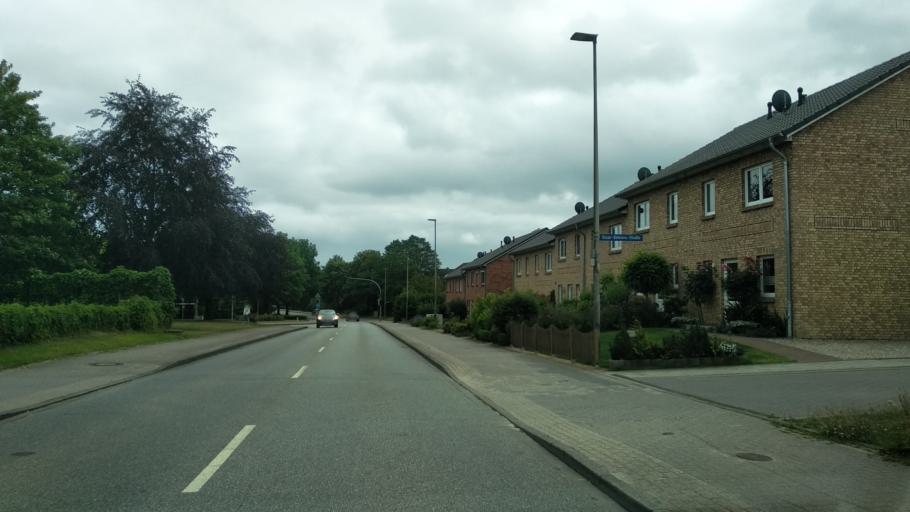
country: DE
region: Schleswig-Holstein
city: Schleswig
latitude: 54.5305
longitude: 9.5570
